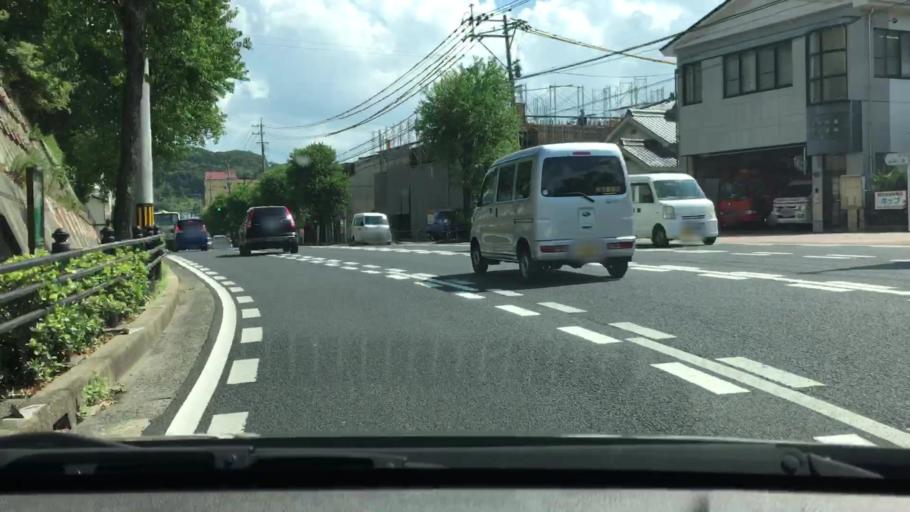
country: JP
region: Nagasaki
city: Sasebo
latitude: 33.2019
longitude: 129.7208
